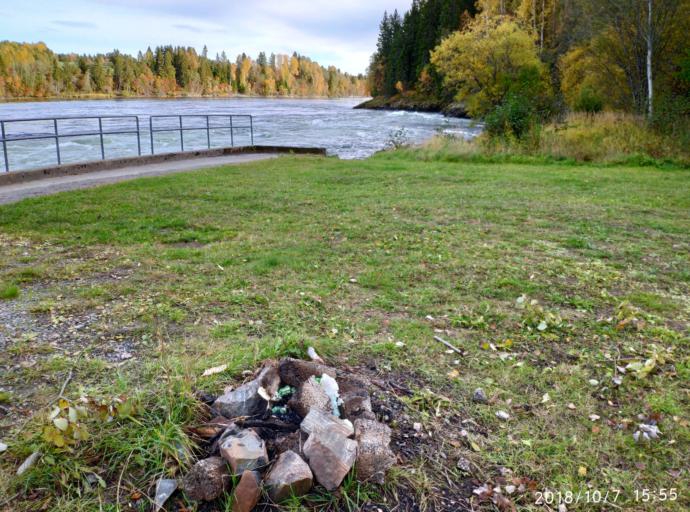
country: NO
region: Akershus
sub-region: Nes
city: Neskollen
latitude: 60.2129
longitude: 11.3564
